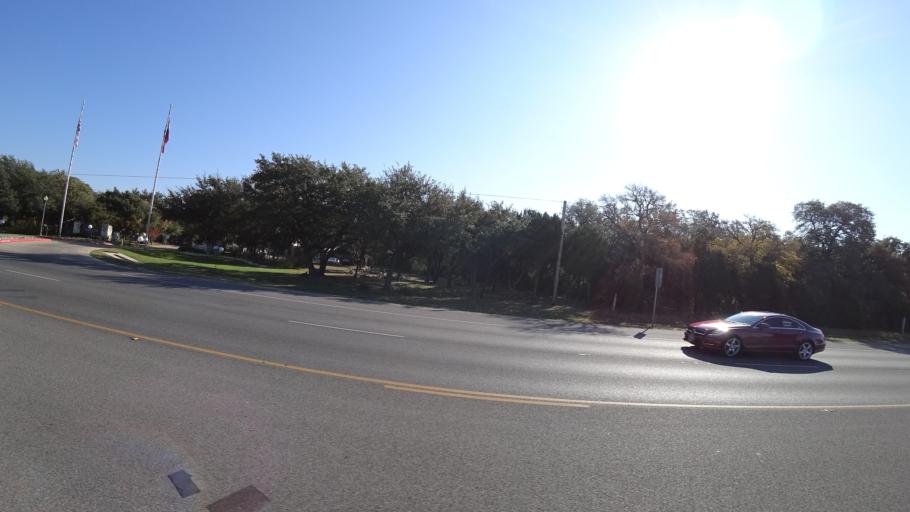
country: US
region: Texas
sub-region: Williamson County
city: Anderson Mill
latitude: 30.4202
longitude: -97.8457
